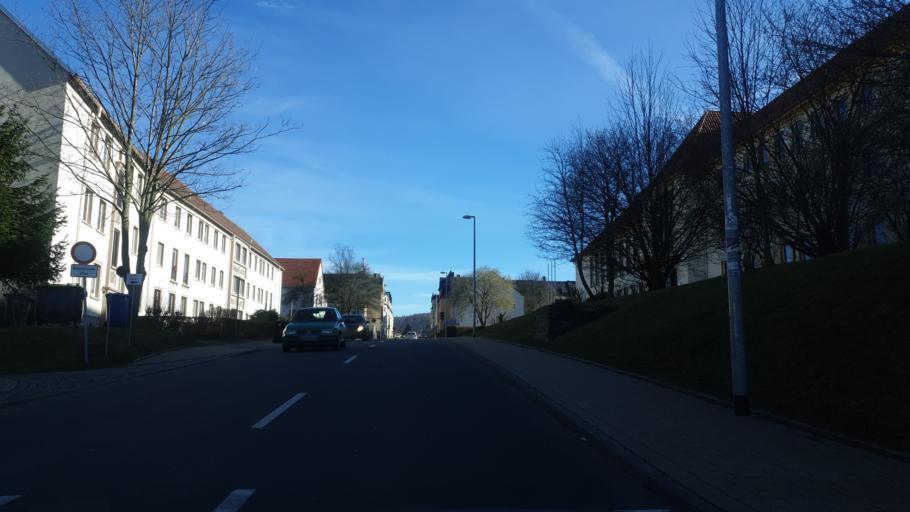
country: DE
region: Saxony
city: Aue
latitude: 50.5941
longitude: 12.7043
